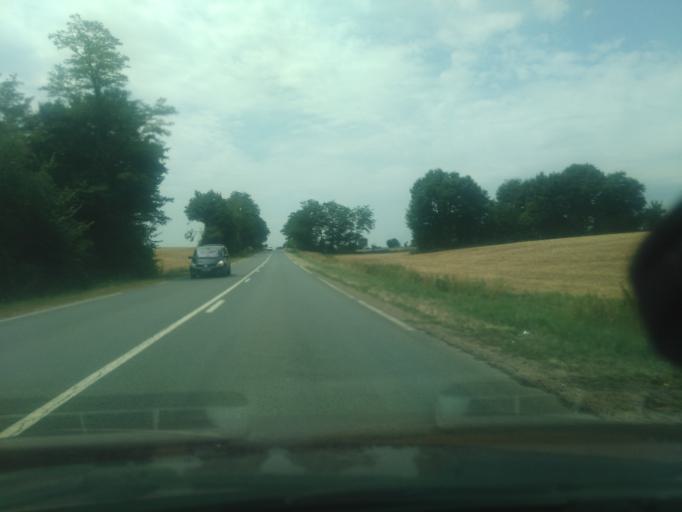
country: FR
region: Poitou-Charentes
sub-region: Departement de la Vienne
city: Saint-Savin
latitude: 46.5743
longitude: 0.9020
